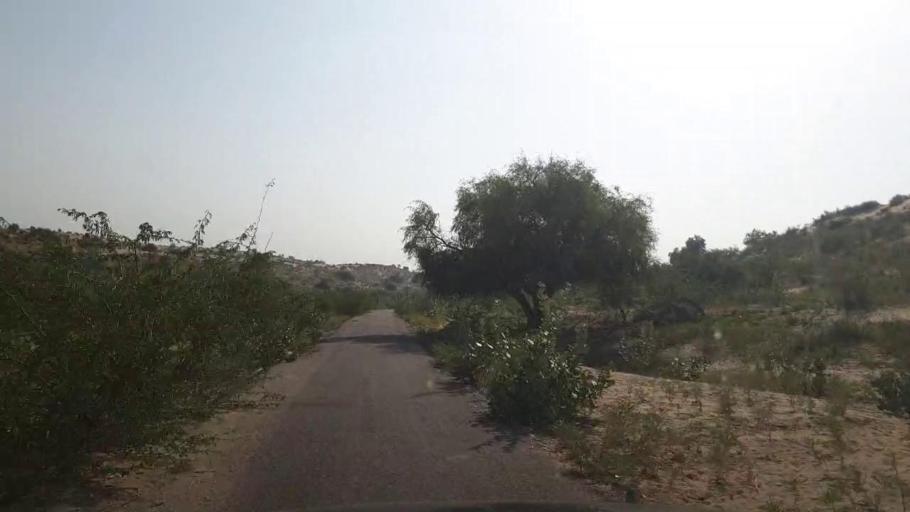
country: PK
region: Sindh
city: Islamkot
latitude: 25.1153
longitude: 70.5095
